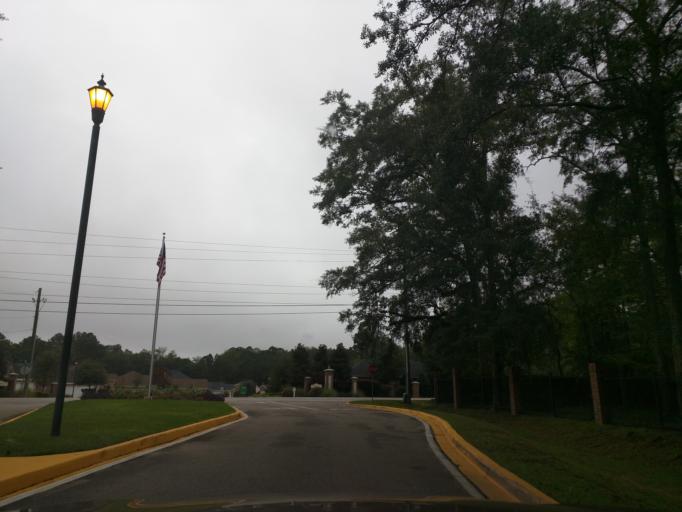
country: US
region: Florida
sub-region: Leon County
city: Tallahassee
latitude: 30.4767
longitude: -84.2098
